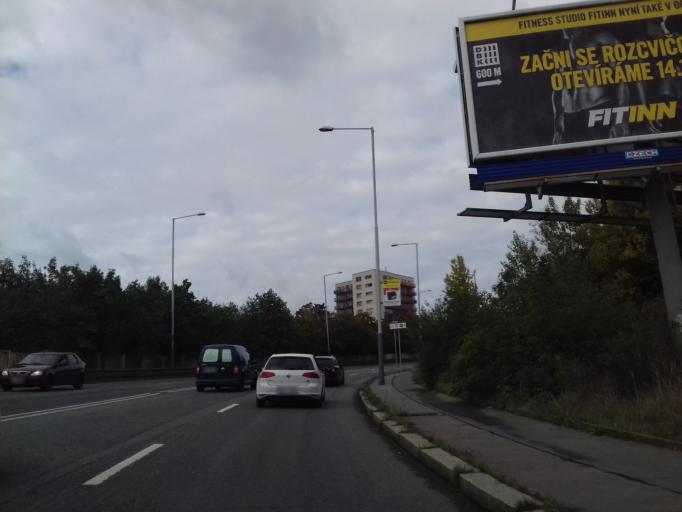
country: CZ
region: Praha
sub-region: Praha 4
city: Hodkovicky
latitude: 50.0392
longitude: 14.4394
